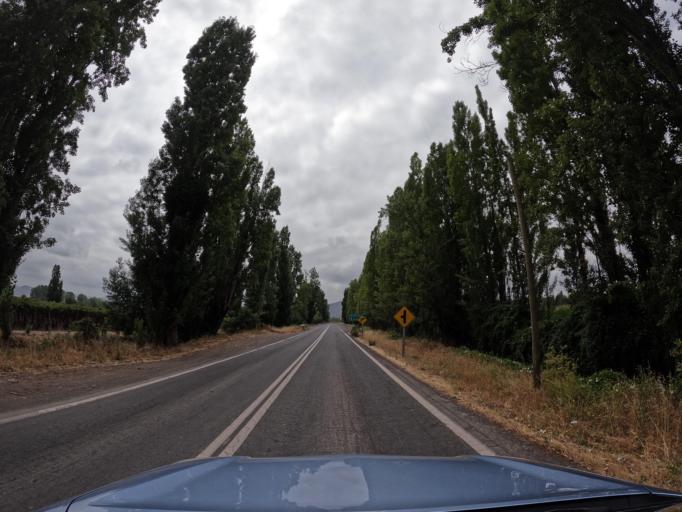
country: CL
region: Maule
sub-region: Provincia de Curico
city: Teno
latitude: -34.7518
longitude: -71.2211
